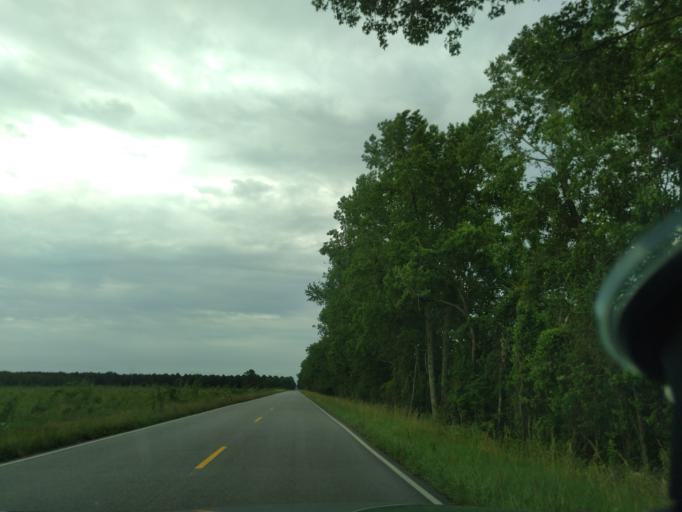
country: US
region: North Carolina
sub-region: Washington County
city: Plymouth
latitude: 35.8617
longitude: -76.5801
